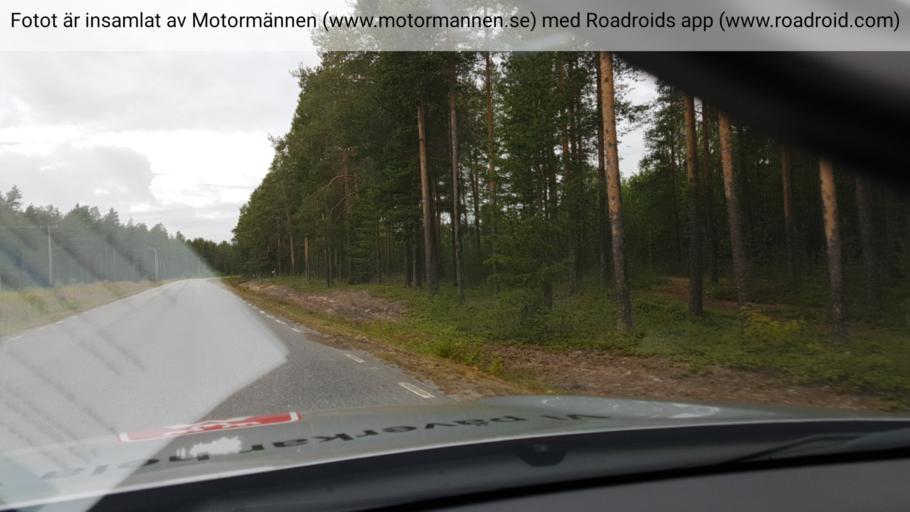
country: SE
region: Norrbotten
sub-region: Bodens Kommun
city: Boden
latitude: 65.8152
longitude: 21.6034
